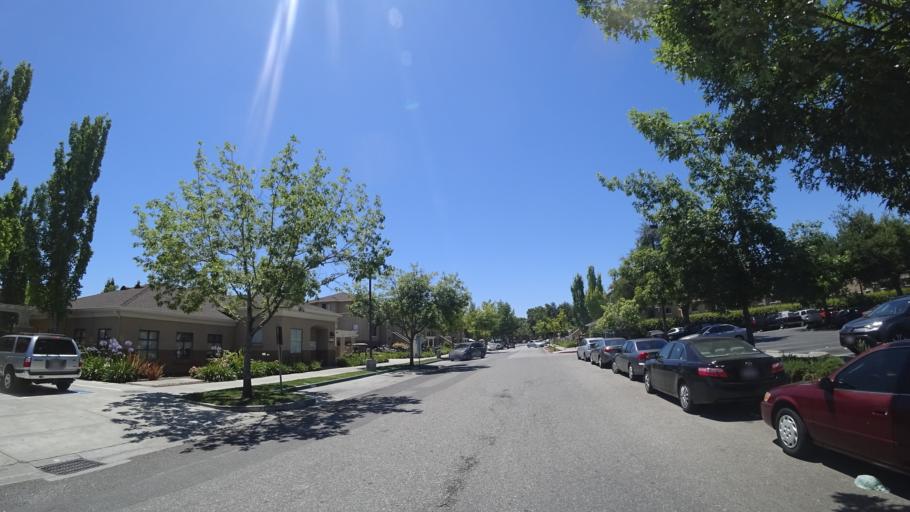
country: US
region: California
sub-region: Santa Clara County
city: Seven Trees
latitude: 37.2576
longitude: -121.8613
